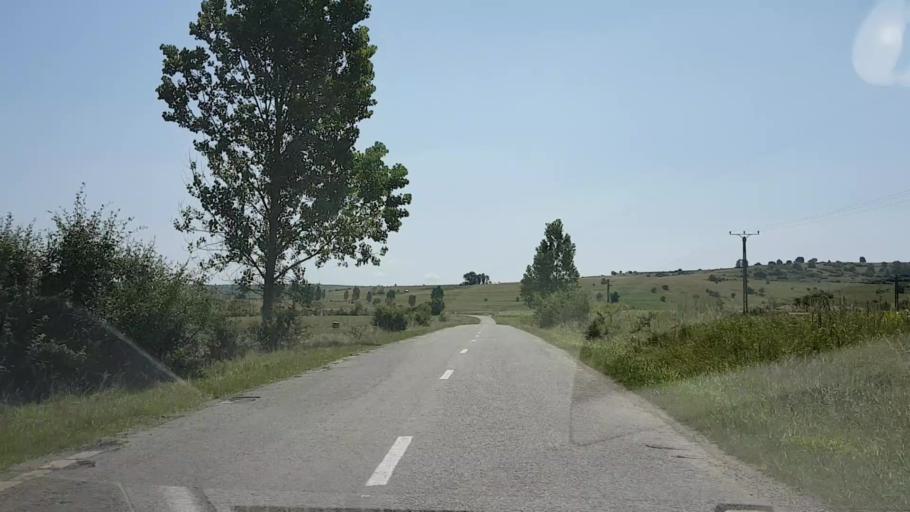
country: RO
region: Sibiu
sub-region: Comuna Merghindeal
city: Merghindeal
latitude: 45.9594
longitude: 24.7578
